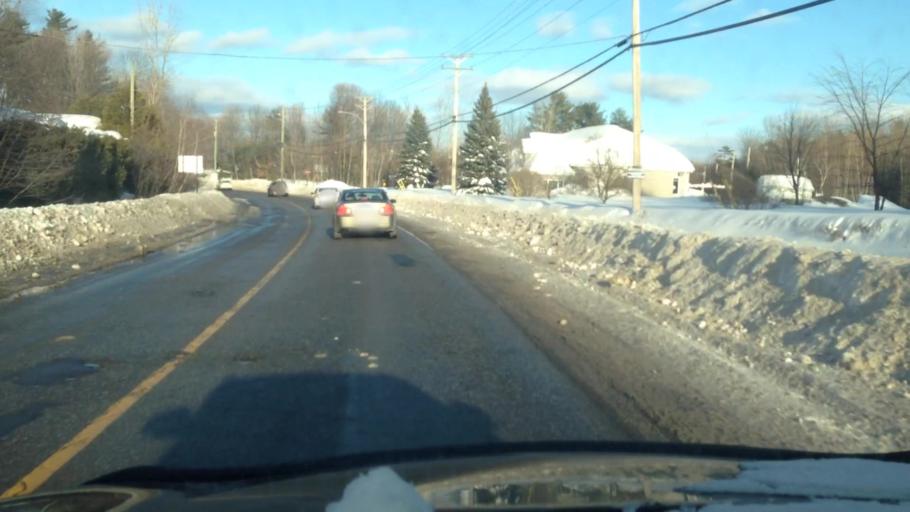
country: CA
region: Quebec
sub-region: Laurentides
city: Saint-Jerome
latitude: 45.7968
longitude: -73.9876
